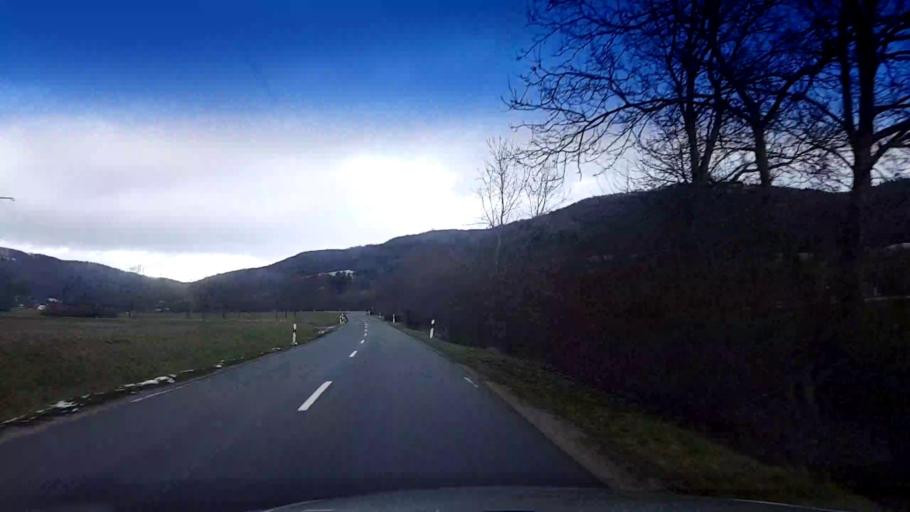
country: DE
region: Bavaria
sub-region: Upper Franconia
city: Buttenheim
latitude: 49.8240
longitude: 11.0788
